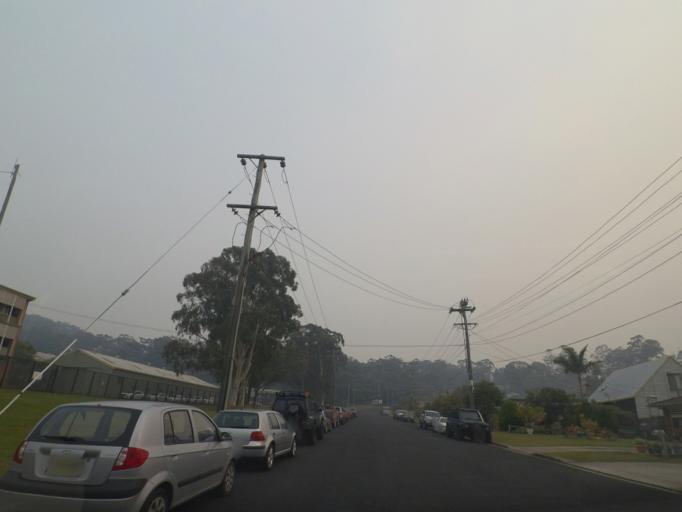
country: AU
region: New South Wales
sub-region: Coffs Harbour
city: Coffs Harbour
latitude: -30.3058
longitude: 153.1032
